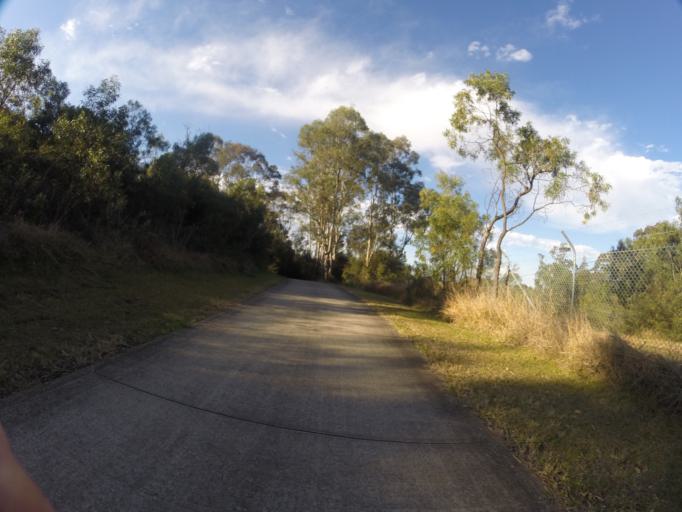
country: AU
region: New South Wales
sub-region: Fairfield
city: Horsley Park
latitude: -33.8484
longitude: 150.8691
